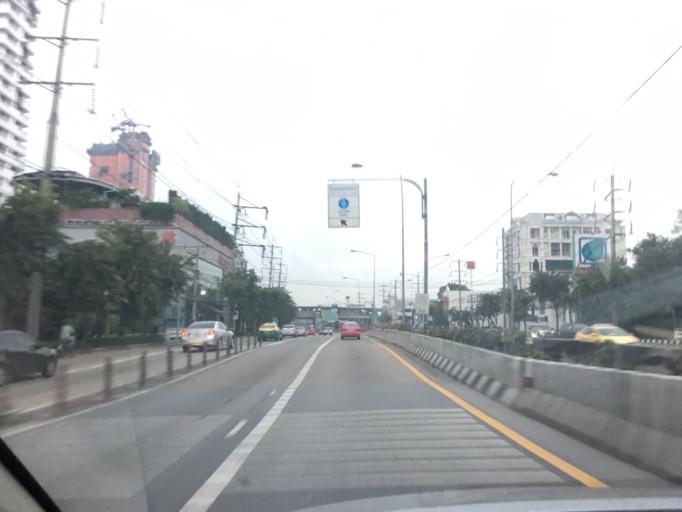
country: TH
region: Bangkok
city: Rat Burana
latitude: 13.6872
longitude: 100.5177
